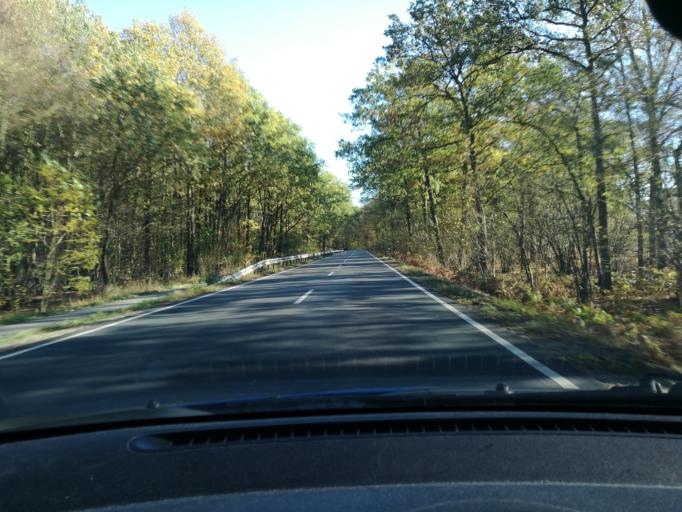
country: DE
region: Lower Saxony
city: Damnatz
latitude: 53.1018
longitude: 11.1570
